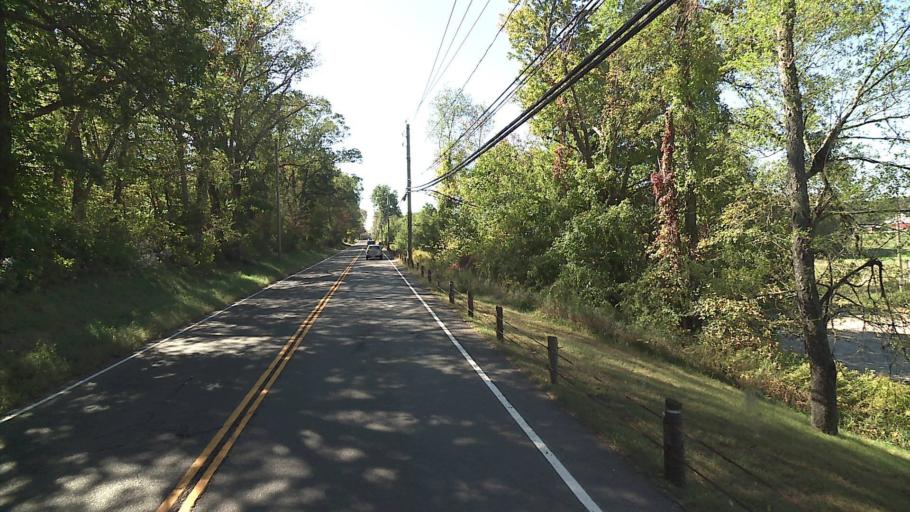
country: US
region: Connecticut
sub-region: Tolland County
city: Ellington
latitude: 41.9361
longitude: -72.4532
